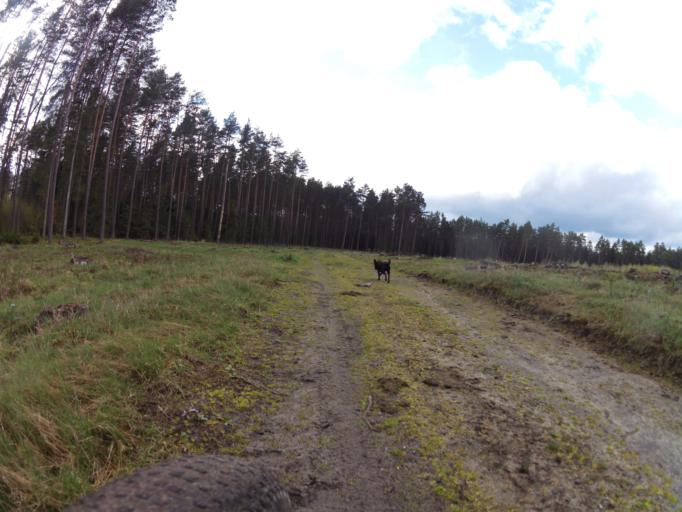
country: PL
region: Pomeranian Voivodeship
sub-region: Powiat slupski
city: Kepice
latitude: 54.3002
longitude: 16.8312
